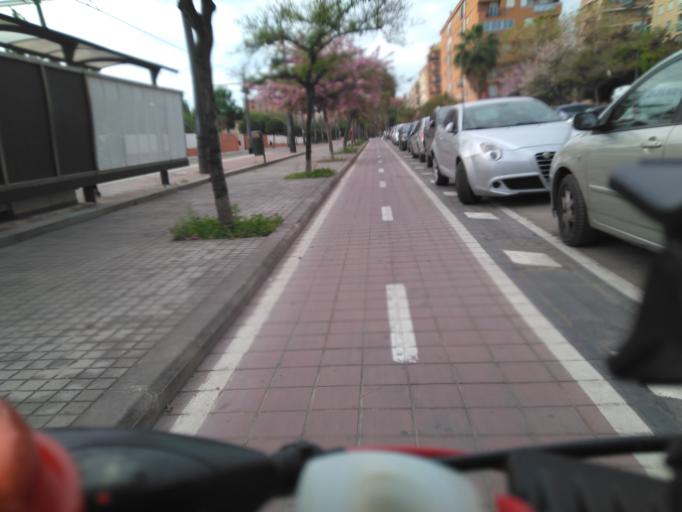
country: ES
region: Valencia
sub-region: Provincia de Valencia
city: Valencia
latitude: 39.4880
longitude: -0.3840
